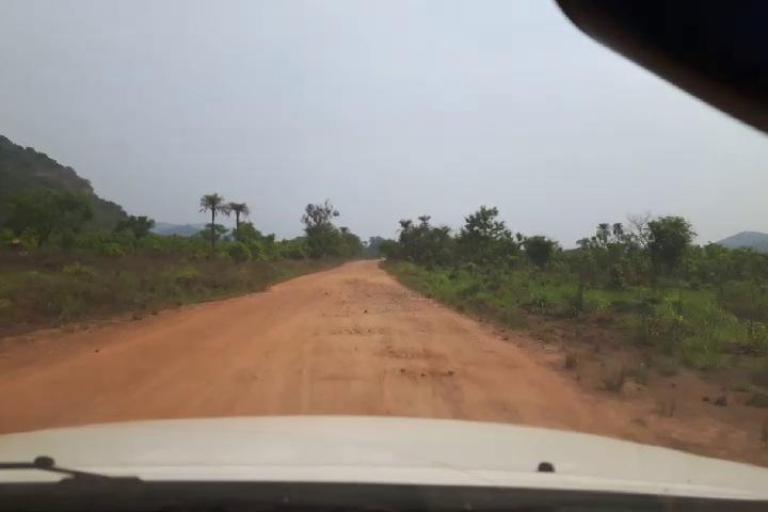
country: SL
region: Northern Province
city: Masingbi
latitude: 8.8857
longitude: -11.8191
